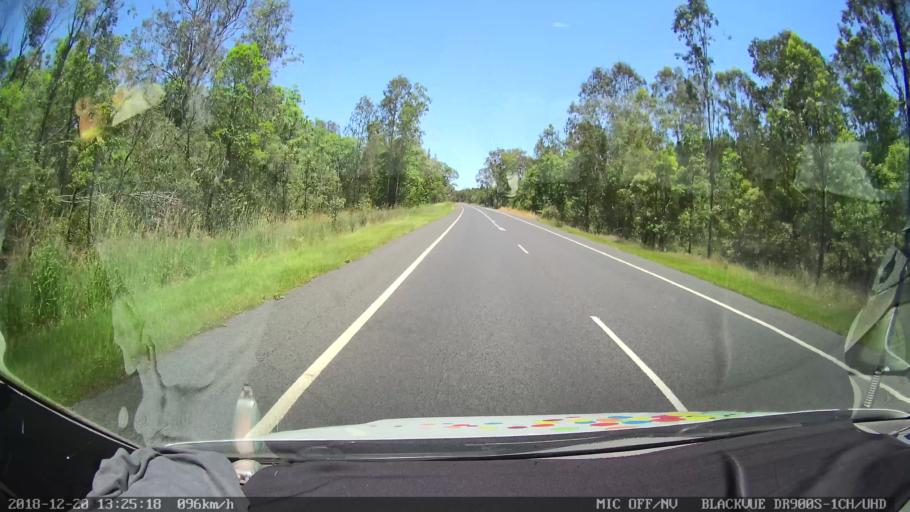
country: AU
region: New South Wales
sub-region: Richmond Valley
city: Casino
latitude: -29.1292
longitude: 152.9969
